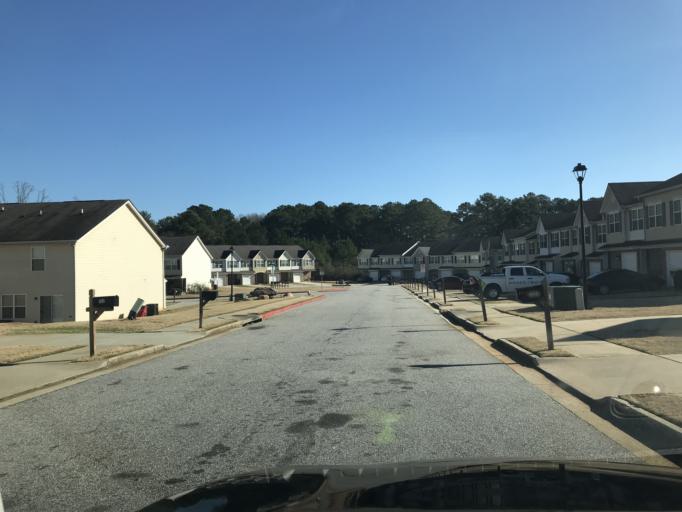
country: US
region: Georgia
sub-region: Clayton County
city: Morrow
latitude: 33.5681
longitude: -84.3661
